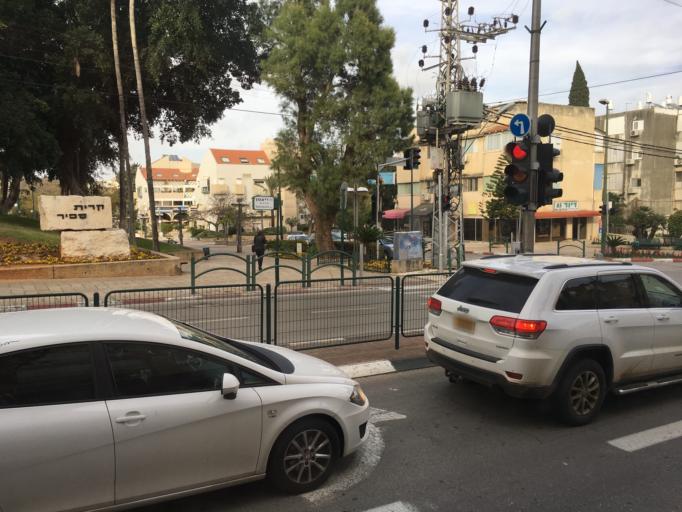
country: IL
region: Central District
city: Kfar Saba
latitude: 32.1759
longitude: 34.9056
